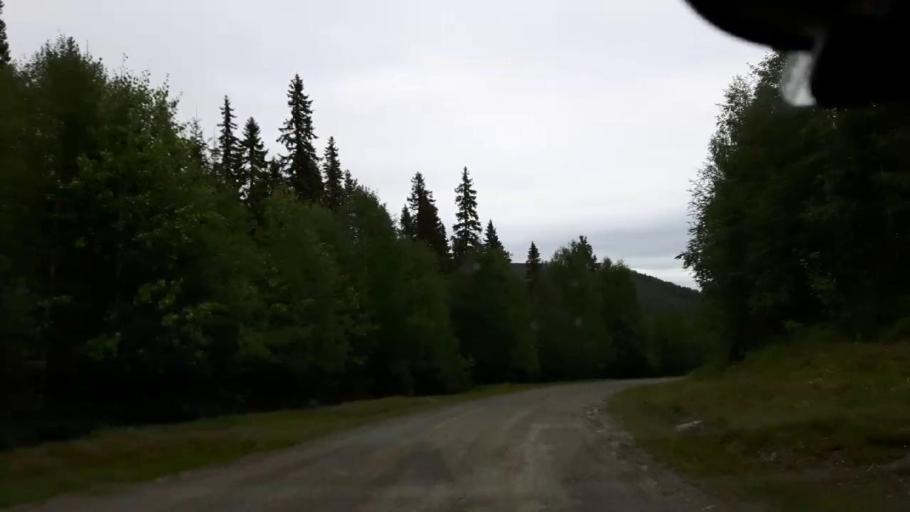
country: SE
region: Vaesternorrland
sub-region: Ange Kommun
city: Ange
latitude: 62.8567
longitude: 15.9103
